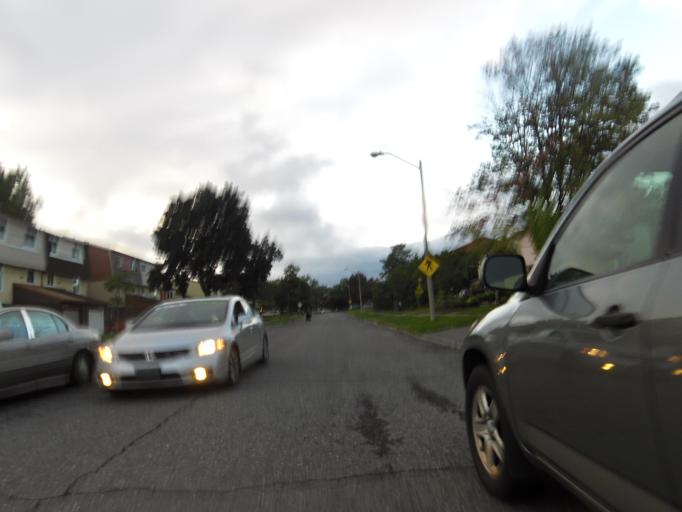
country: CA
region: Ontario
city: Bells Corners
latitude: 45.3479
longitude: -75.7984
